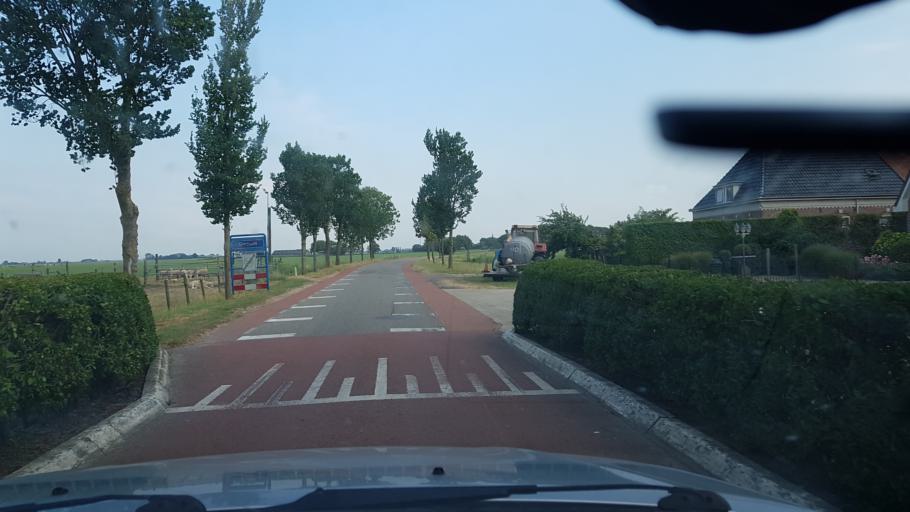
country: NL
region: Friesland
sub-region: Gemeente Ferwerderadiel
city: Burdaard
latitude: 53.3218
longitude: 5.8748
